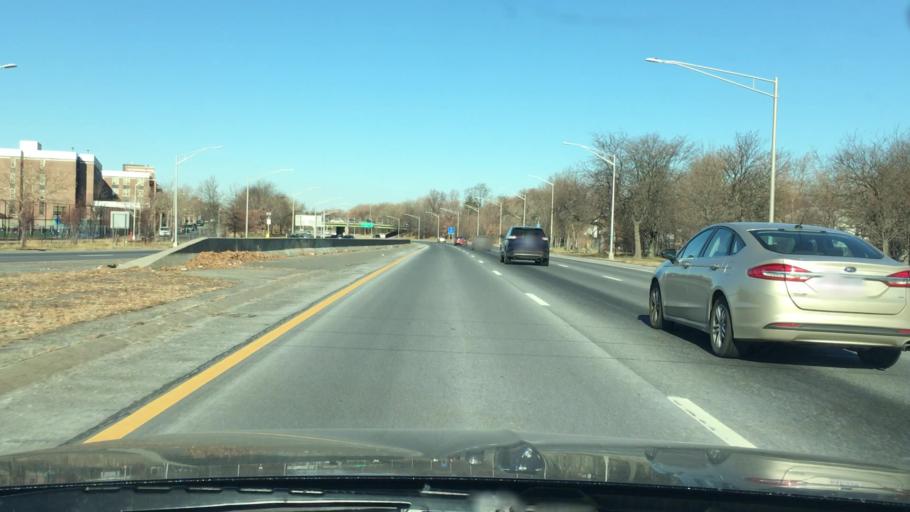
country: US
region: New York
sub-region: Bronx
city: The Bronx
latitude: 40.8251
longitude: -73.8163
